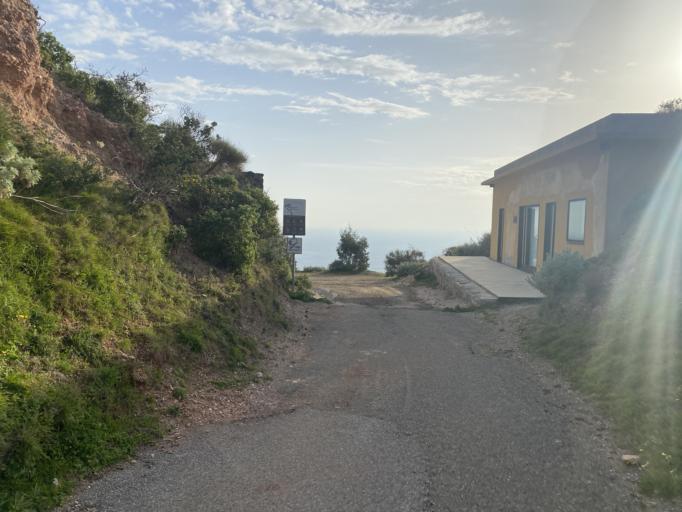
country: IT
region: Sicily
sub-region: Messina
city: Pianoconte
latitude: 38.4968
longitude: 14.9100
